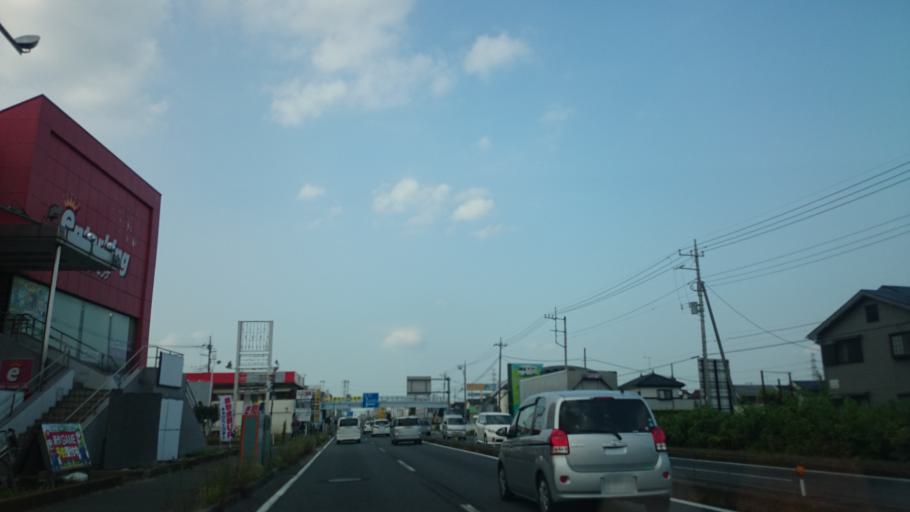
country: JP
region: Saitama
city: Kasukabe
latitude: 35.9653
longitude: 139.7332
